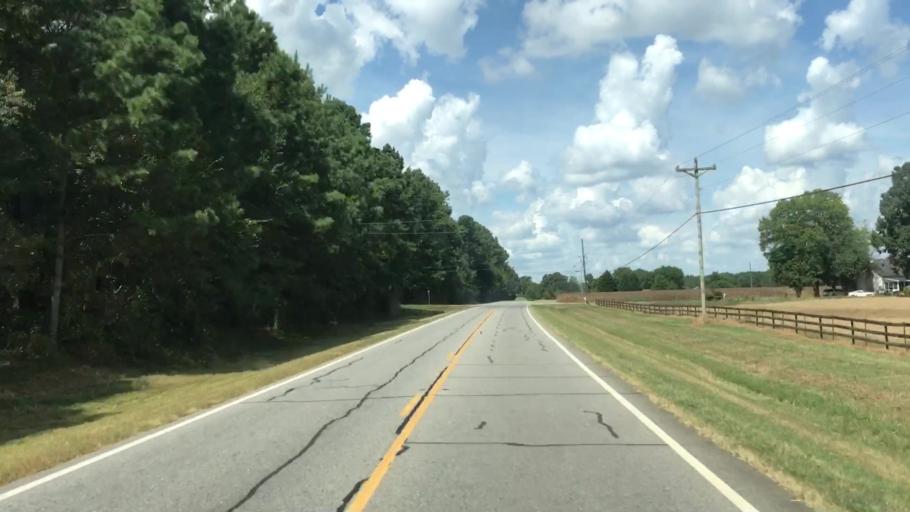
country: US
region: Georgia
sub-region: Oconee County
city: Watkinsville
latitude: 33.8125
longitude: -83.3580
